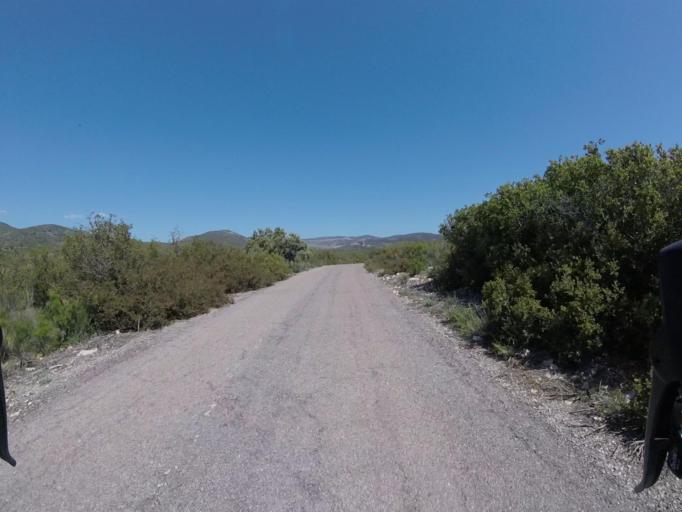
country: ES
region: Valencia
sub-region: Provincia de Castello
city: Sierra-Engarceran
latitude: 40.2388
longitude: -0.0270
